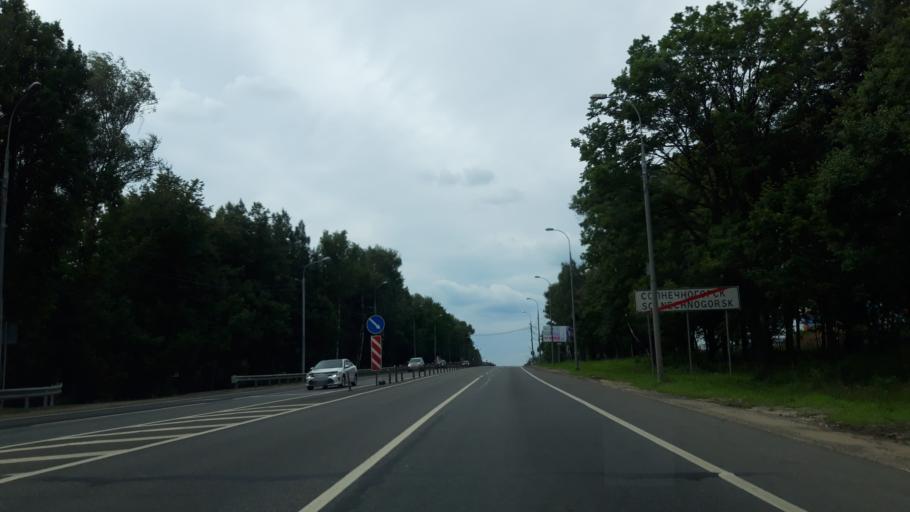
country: RU
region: Moskovskaya
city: Solnechnogorsk
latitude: 56.2005
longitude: 36.9570
